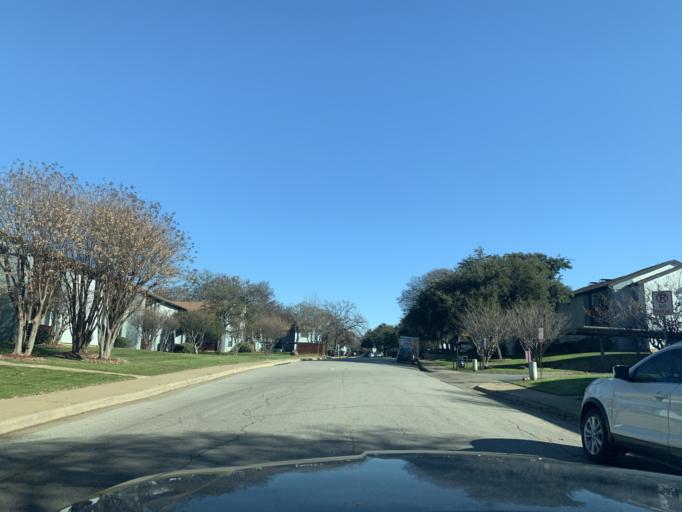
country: US
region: Texas
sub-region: Tarrant County
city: Bedford
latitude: 32.8331
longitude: -97.1418
